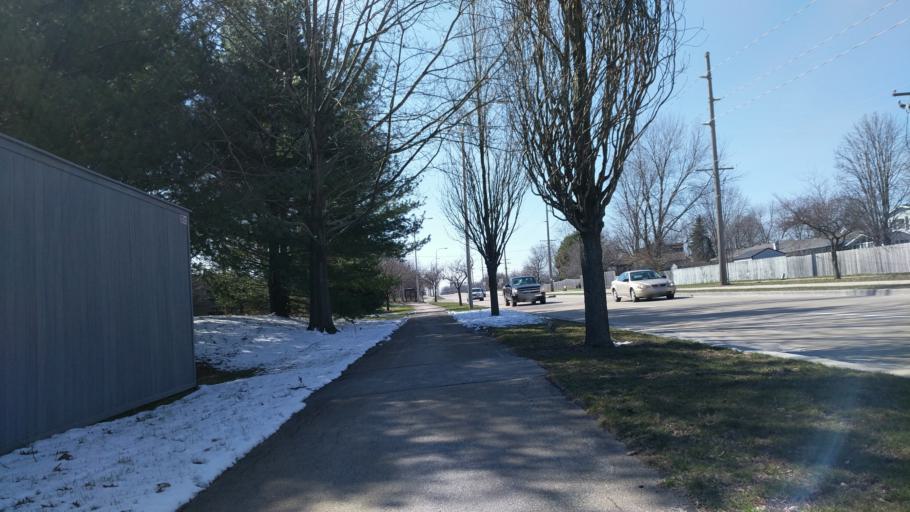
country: US
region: Illinois
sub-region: Champaign County
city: Urbana
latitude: 40.0837
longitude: -88.2056
